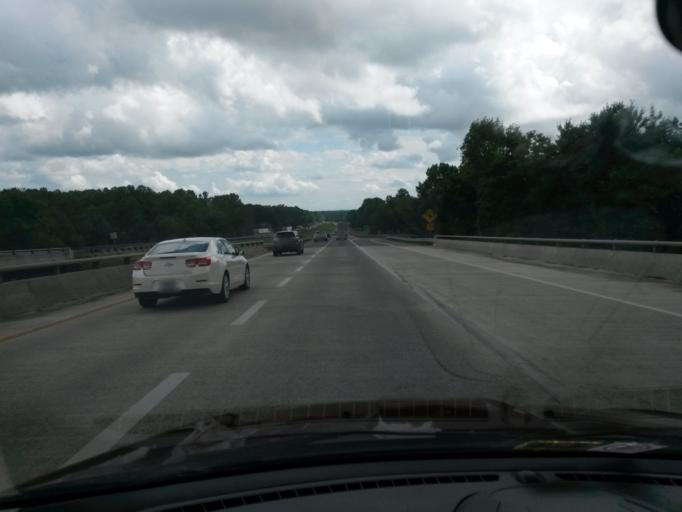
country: US
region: Virginia
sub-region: Carroll County
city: Cana
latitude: 36.5785
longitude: -80.7431
